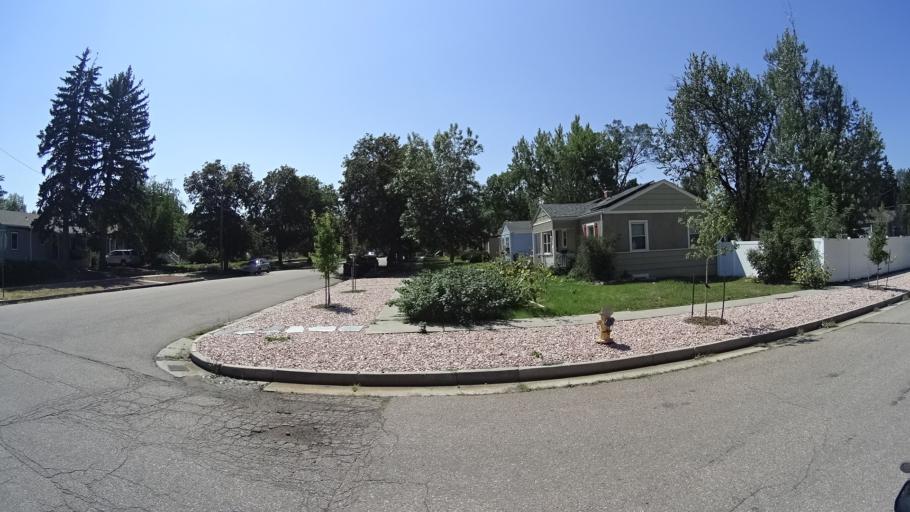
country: US
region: Colorado
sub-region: El Paso County
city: Colorado Springs
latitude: 38.8511
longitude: -104.8045
